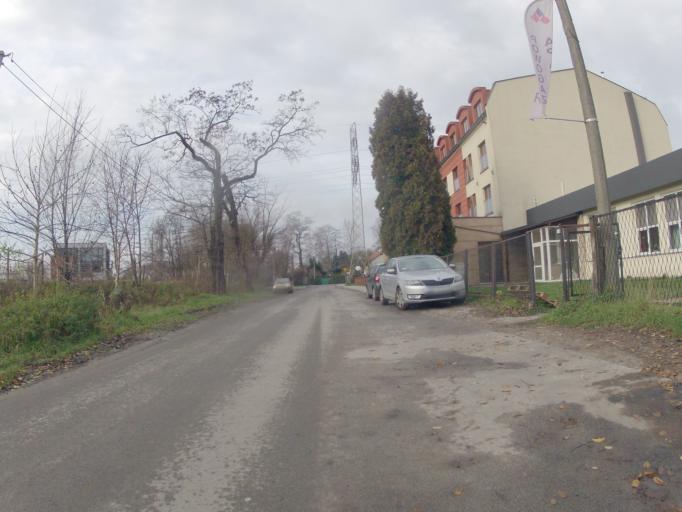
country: PL
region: Lesser Poland Voivodeship
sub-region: Powiat krakowski
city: Rzaska
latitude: 50.0814
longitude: 19.8496
